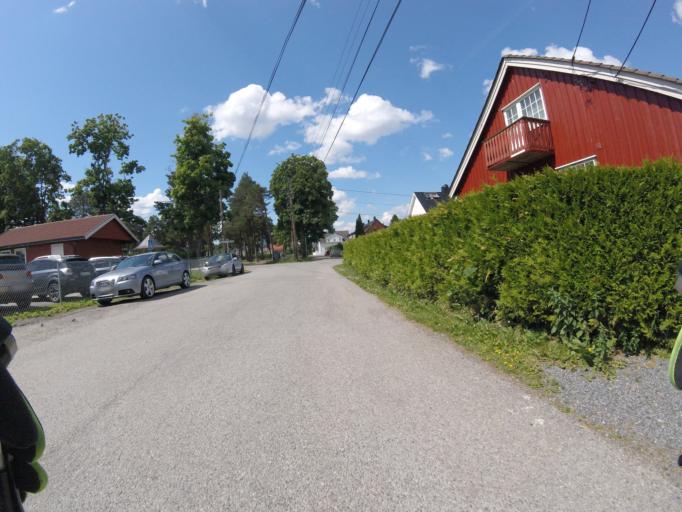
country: NO
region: Akershus
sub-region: Skedsmo
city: Lillestrom
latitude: 59.9543
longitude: 11.0630
